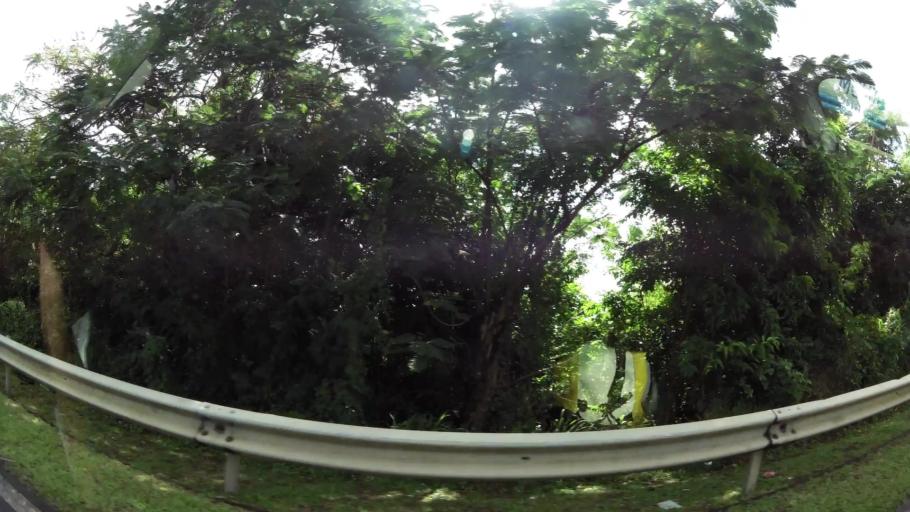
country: MQ
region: Martinique
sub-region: Martinique
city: Sainte-Luce
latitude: 14.5018
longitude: -60.9807
